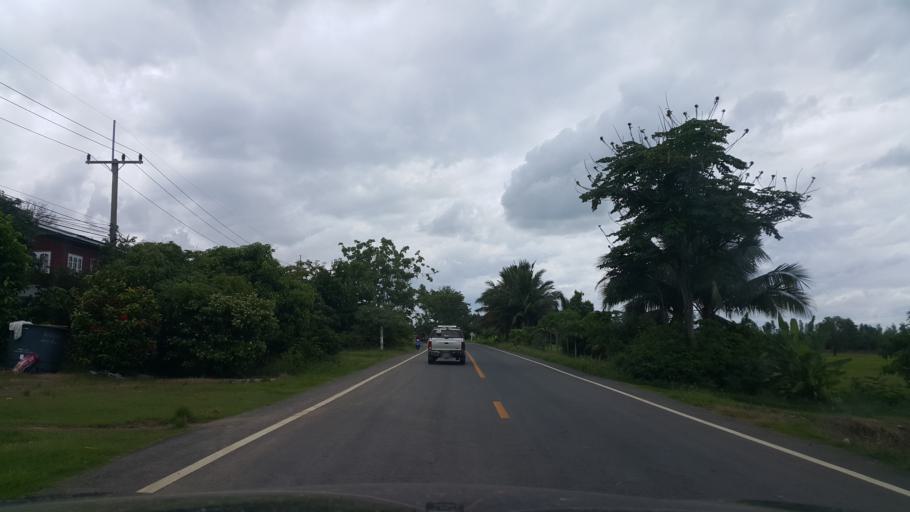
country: TH
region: Sukhothai
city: Sukhothai
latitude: 16.9173
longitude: 99.8570
